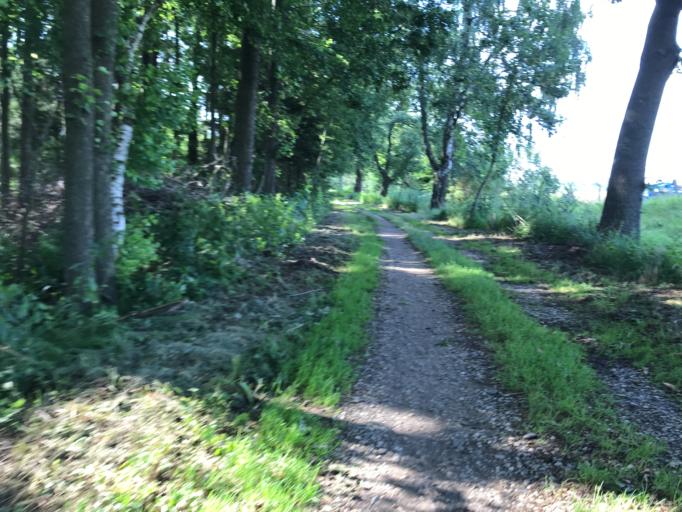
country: CZ
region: Jihocesky
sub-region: Okres Jindrichuv Hradec
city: Trebon
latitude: 49.0187
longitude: 14.7635
